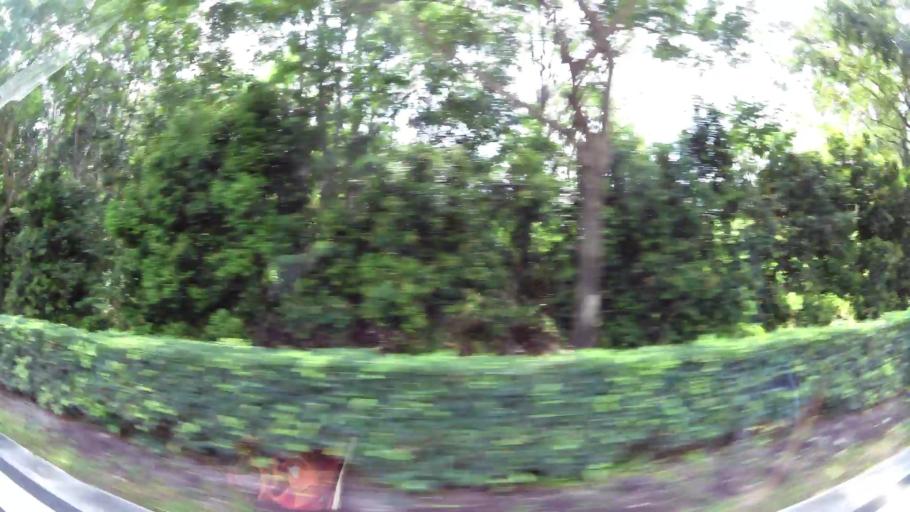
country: SG
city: Singapore
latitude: 1.3320
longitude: 103.7675
